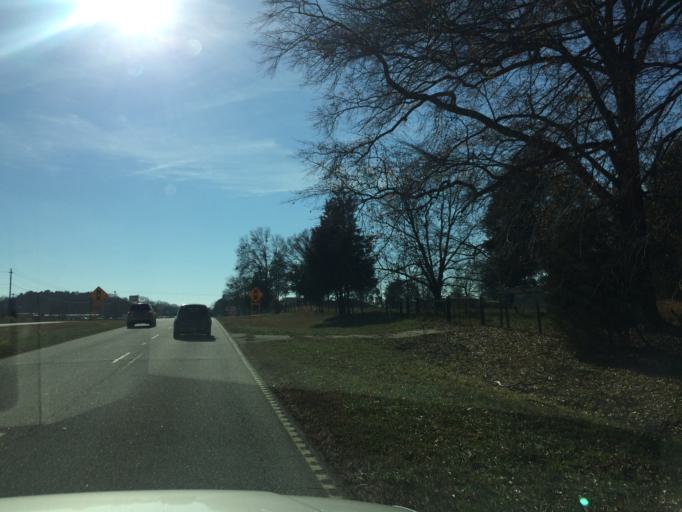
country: US
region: South Carolina
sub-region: Greenwood County
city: Greenwood
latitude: 34.2604
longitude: -82.0871
